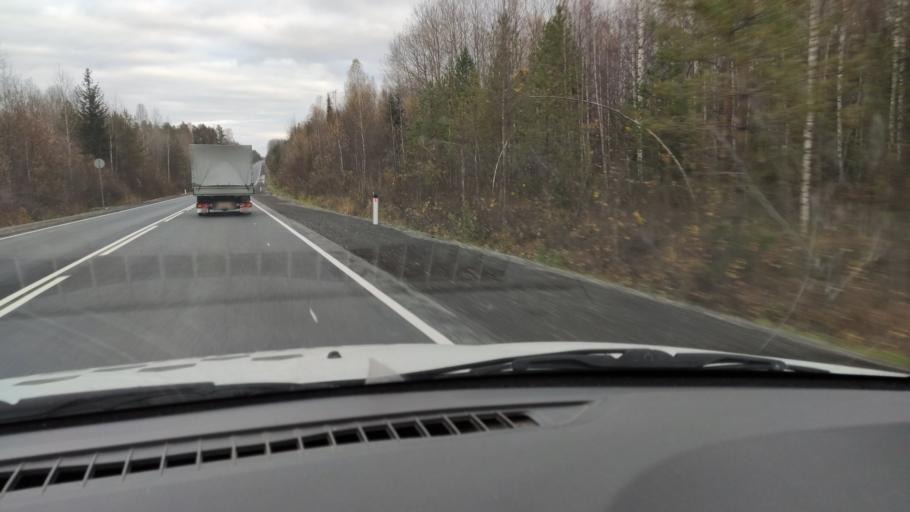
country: RU
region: Kirov
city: Chernaya Kholunitsa
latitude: 58.8726
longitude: 51.5196
